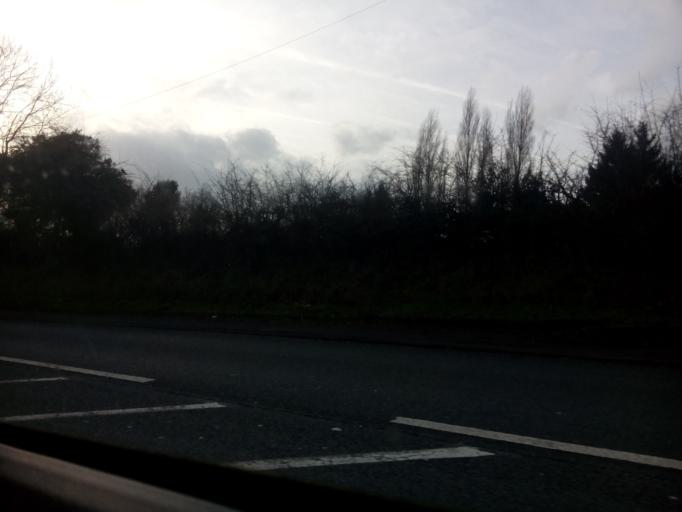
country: GB
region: England
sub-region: Worcestershire
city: Bromsgrove
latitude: 52.3693
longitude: -2.0461
